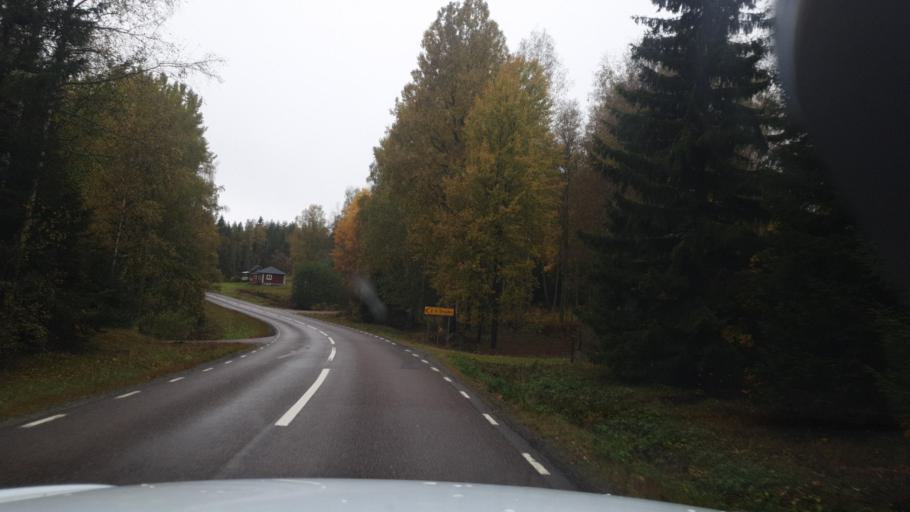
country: SE
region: Vaermland
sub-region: Eda Kommun
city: Amotfors
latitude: 59.6329
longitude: 12.3484
